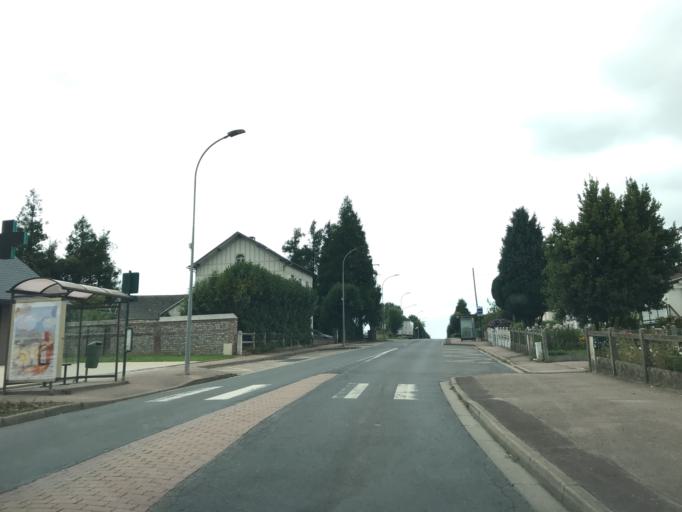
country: FR
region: Haute-Normandie
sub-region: Departement de la Seine-Maritime
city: Breaute
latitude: 49.6276
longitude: 0.3975
